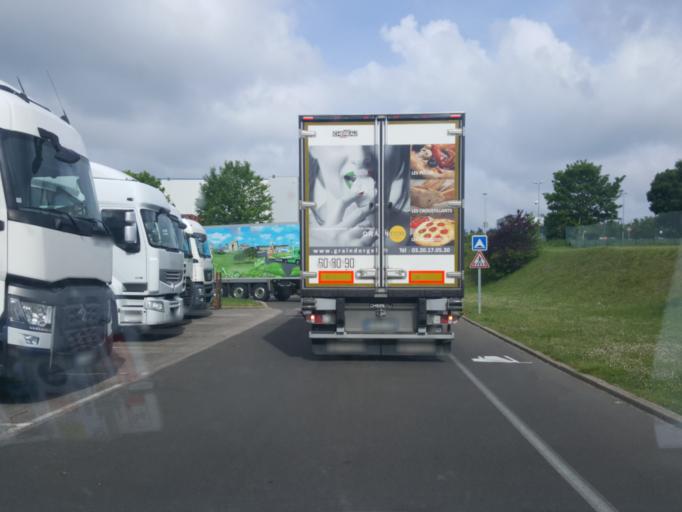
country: FR
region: Haute-Normandie
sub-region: Departement de l'Eure
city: Saint-Pierre-du-Vauvray
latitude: 49.2012
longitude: 1.2201
